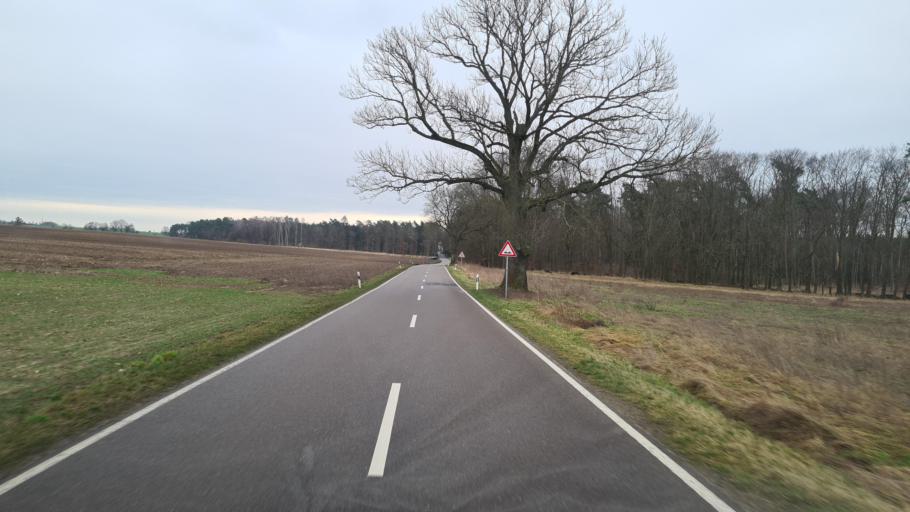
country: DE
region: Brandenburg
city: Gransee
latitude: 52.9385
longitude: 13.2303
